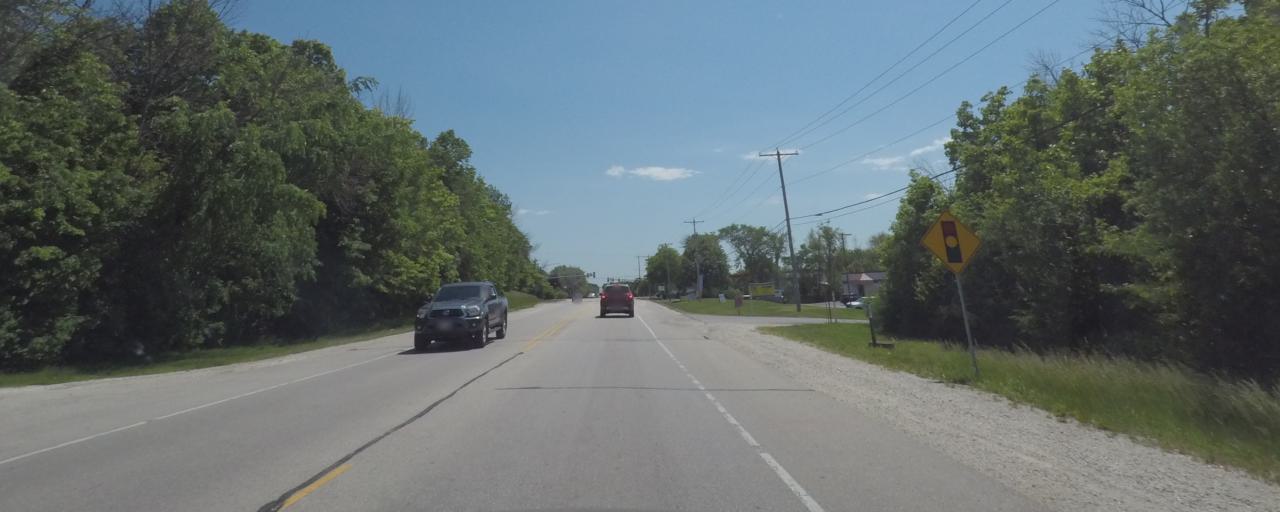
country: US
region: Wisconsin
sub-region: Waukesha County
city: New Berlin
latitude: 42.9961
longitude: -88.1279
